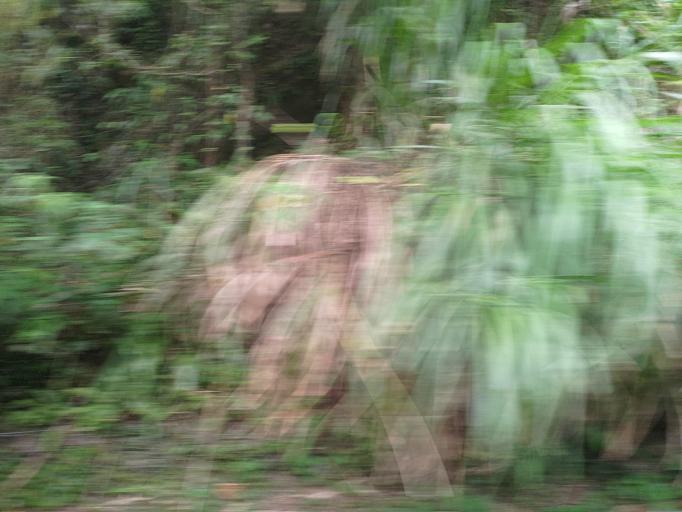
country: TW
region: Taiwan
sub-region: Hsinchu
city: Hsinchu
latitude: 24.6018
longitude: 121.0378
